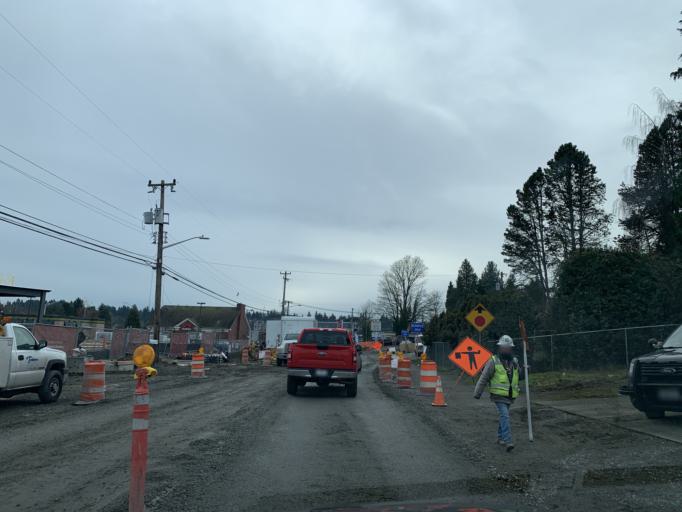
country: US
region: Washington
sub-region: King County
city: Riverton
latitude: 47.4684
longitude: -122.2892
